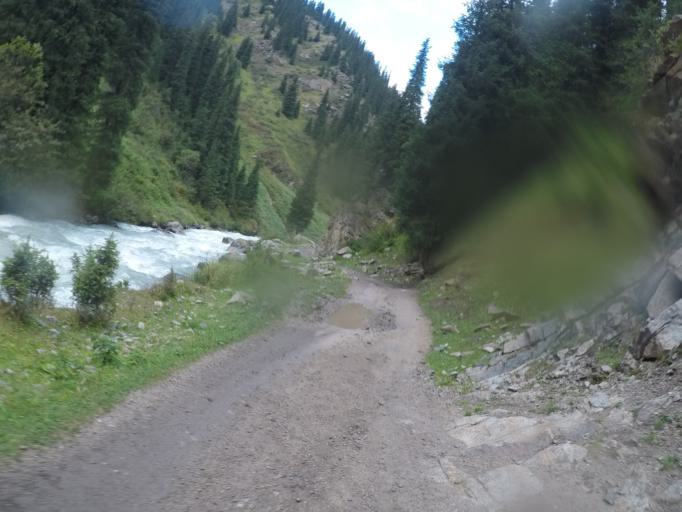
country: KG
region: Ysyk-Koel
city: Teploklyuchenka
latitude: 42.4142
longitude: 78.5720
